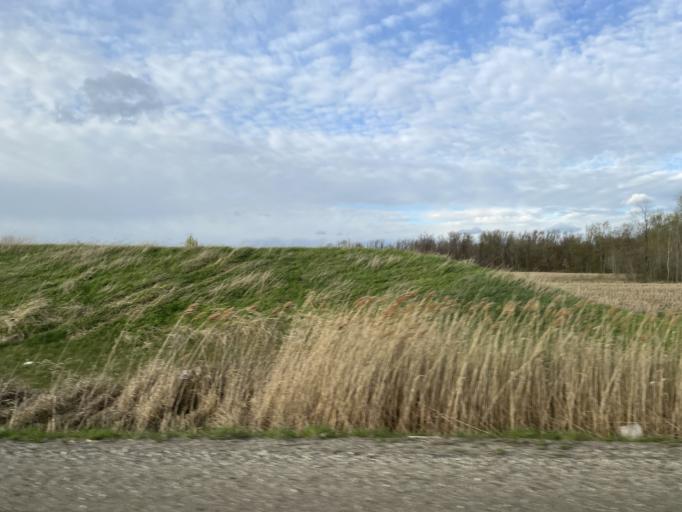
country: CA
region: Ontario
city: Waterloo
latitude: 43.4788
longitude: -80.4046
